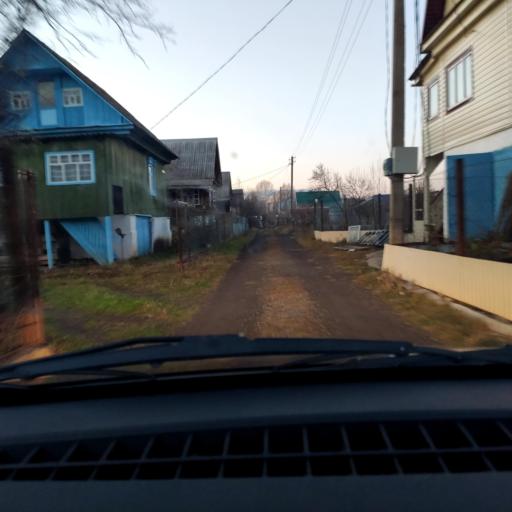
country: RU
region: Bashkortostan
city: Ufa
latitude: 54.6488
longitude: 55.8989
